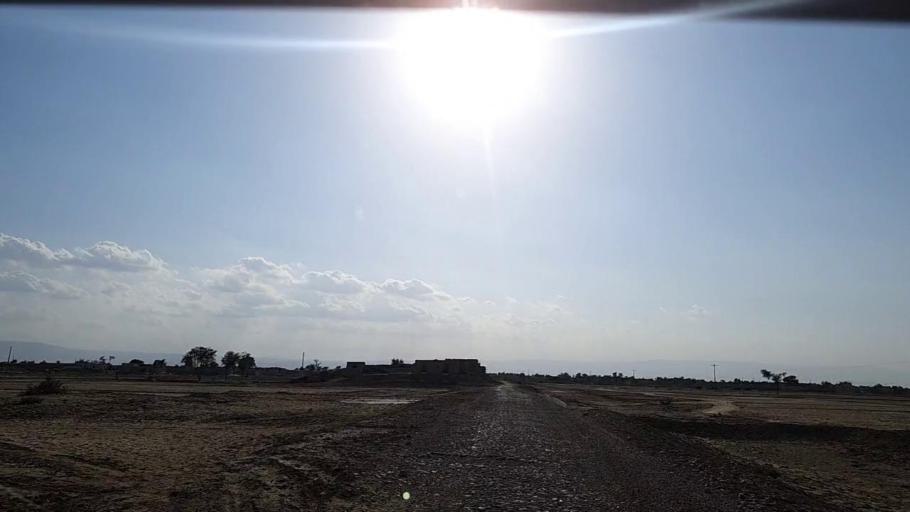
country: PK
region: Sindh
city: Johi
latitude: 26.5848
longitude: 67.5481
